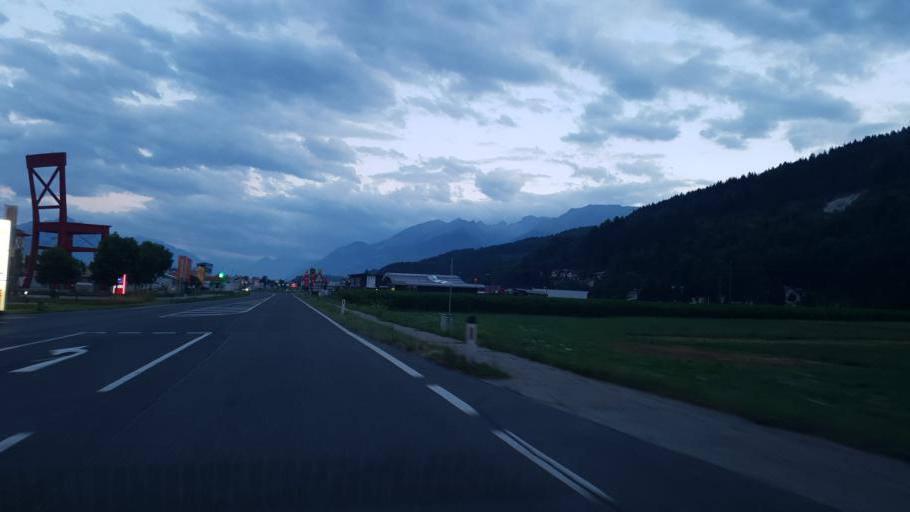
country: AT
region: Carinthia
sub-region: Politischer Bezirk Spittal an der Drau
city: Spittal an der Drau
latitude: 46.7852
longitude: 13.5259
